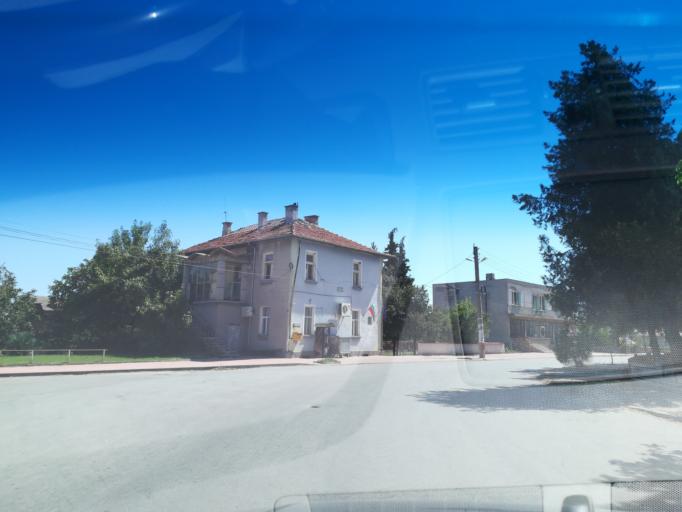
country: BG
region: Pazardzhik
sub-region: Obshtina Pazardzhik
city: Pazardzhik
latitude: 42.3326
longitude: 24.4022
